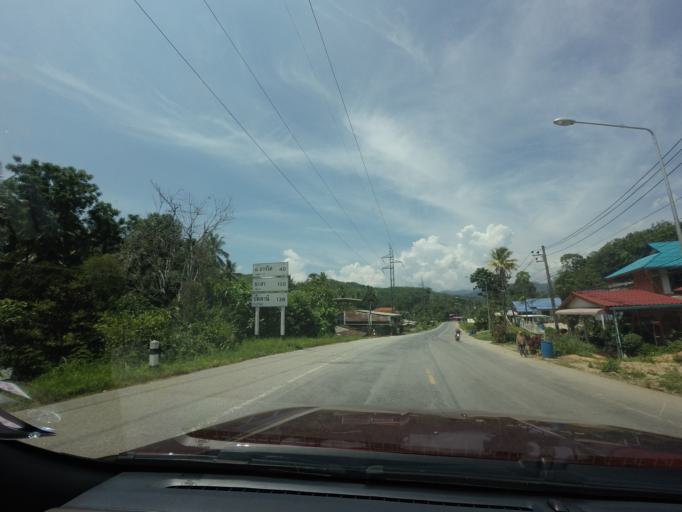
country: TH
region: Yala
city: Betong
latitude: 5.9213
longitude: 101.1655
